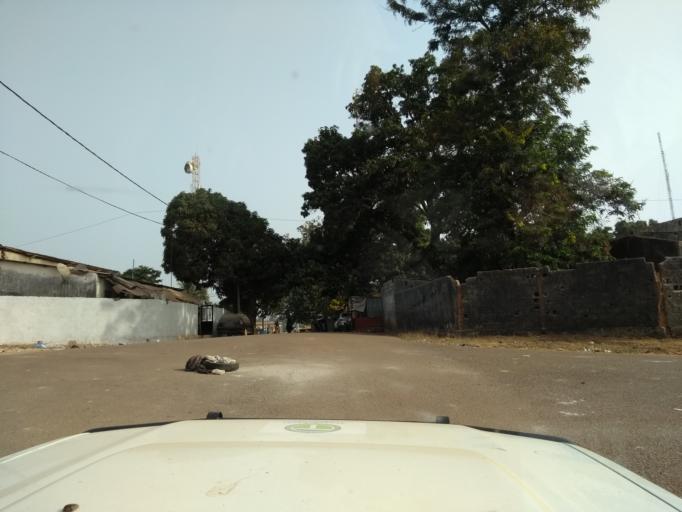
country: GN
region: Kindia
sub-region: Prefecture de Dubreka
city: Dubreka
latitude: 9.7889
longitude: -13.5220
